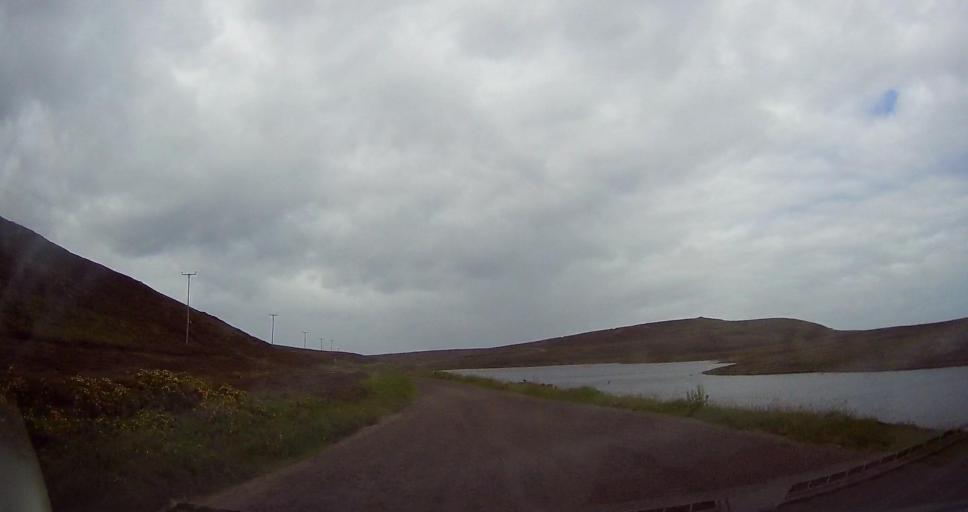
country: GB
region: Scotland
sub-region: Highland
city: Thurso
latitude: 58.6608
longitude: -3.3717
